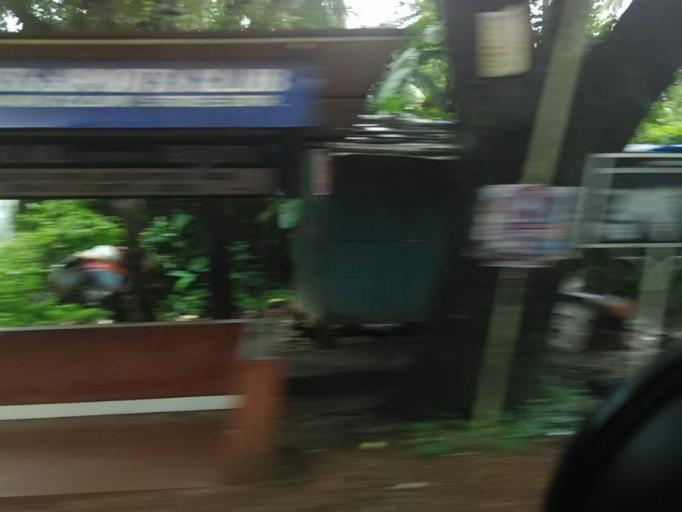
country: IN
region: Kerala
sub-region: Kozhikode
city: Kozhikode
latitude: 11.2754
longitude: 75.8128
